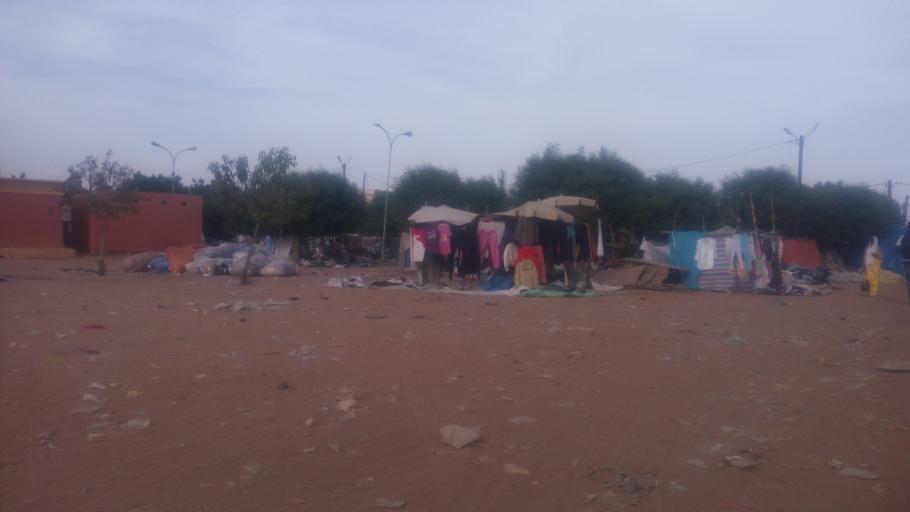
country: SN
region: Diourbel
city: Touba
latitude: 14.8649
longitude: -15.8787
